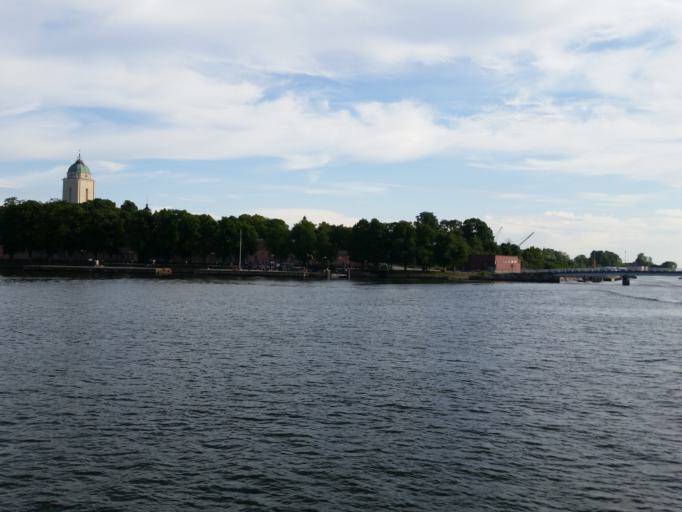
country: FI
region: Uusimaa
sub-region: Helsinki
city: Helsinki
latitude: 60.1513
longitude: 24.9839
